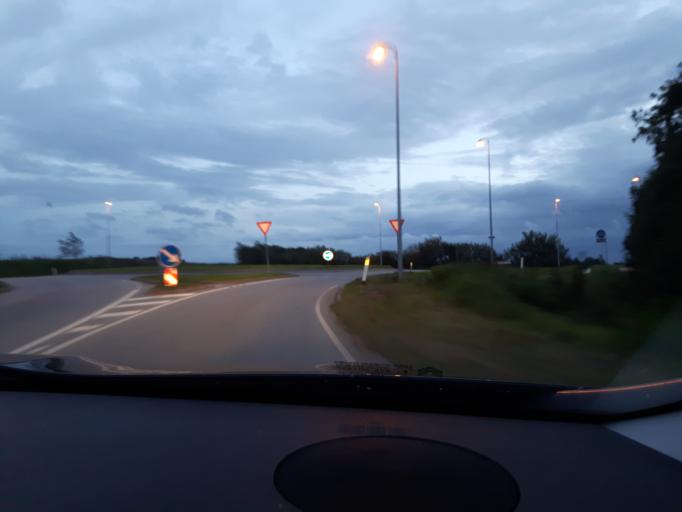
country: DK
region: North Denmark
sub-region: Hjorring Kommune
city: Hjorring
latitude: 57.4618
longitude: 9.9502
